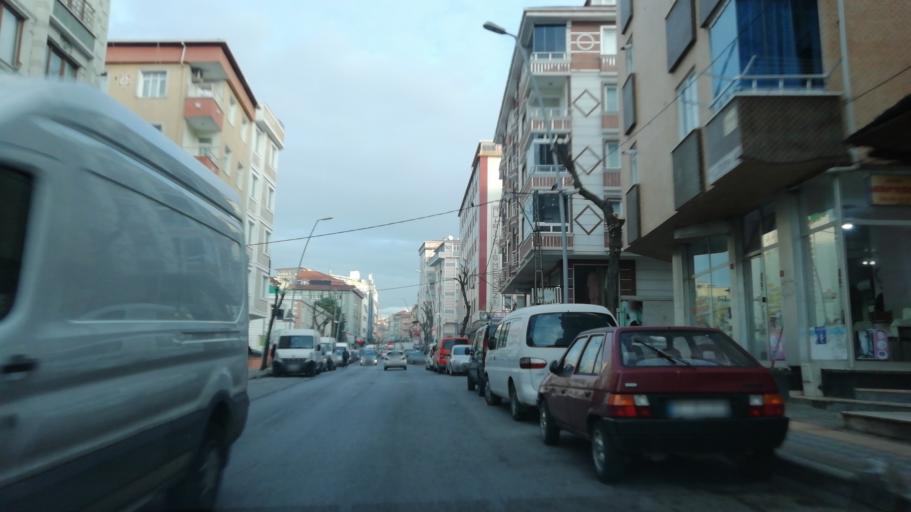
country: TR
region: Istanbul
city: Bahcelievler
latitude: 40.9996
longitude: 28.8271
